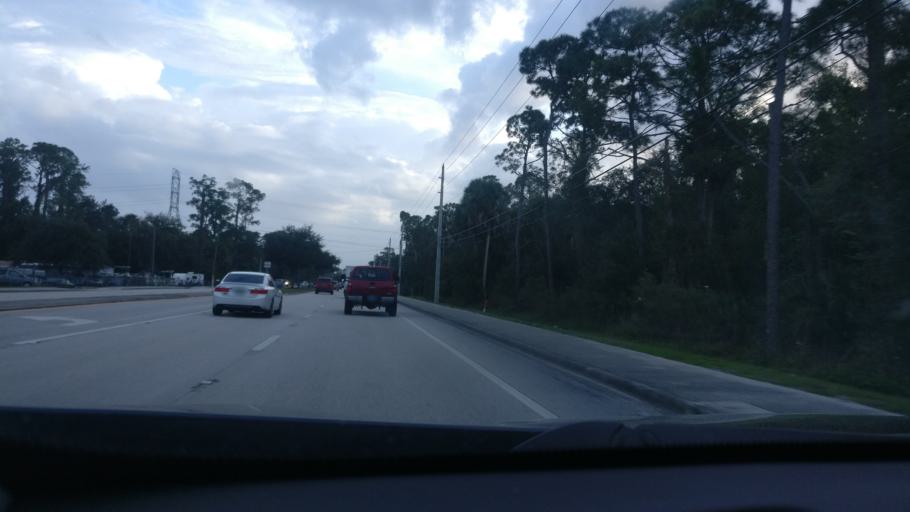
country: US
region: Florida
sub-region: Volusia County
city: DeBary
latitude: 28.8514
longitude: -81.3223
